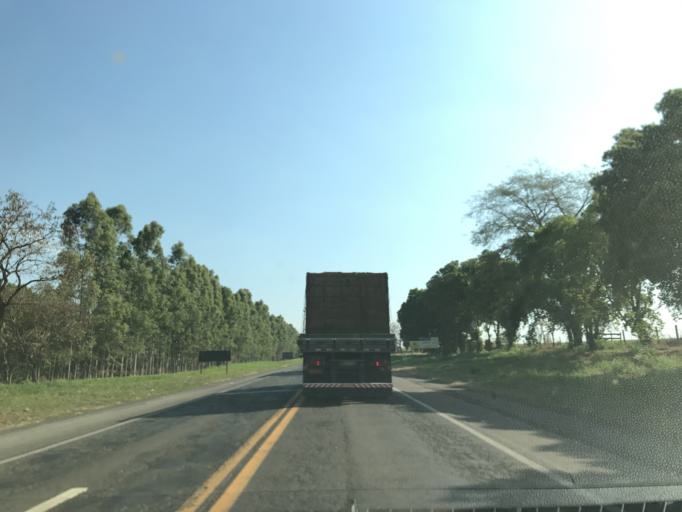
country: BR
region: Sao Paulo
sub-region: Penapolis
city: Penapolis
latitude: -21.4453
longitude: -50.1522
